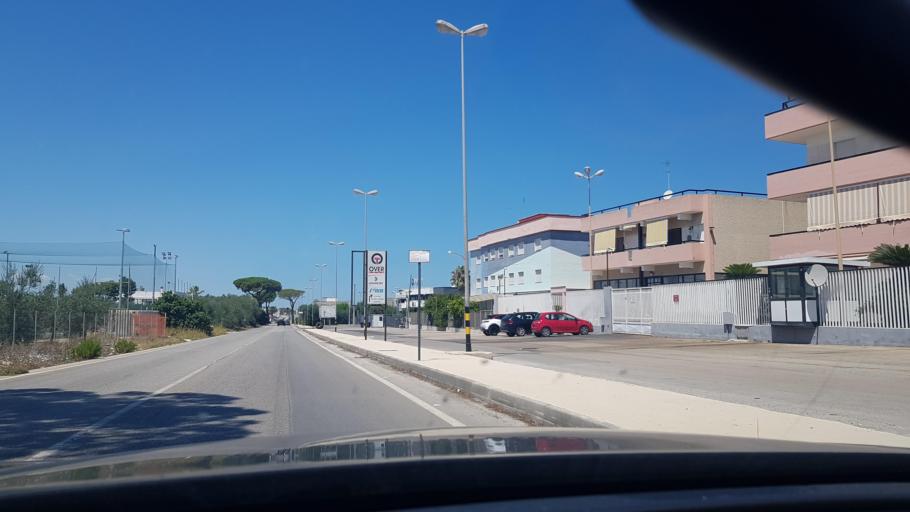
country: IT
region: Apulia
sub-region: Provincia di Barletta - Andria - Trani
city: Barletta
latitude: 41.3043
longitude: 16.3202
